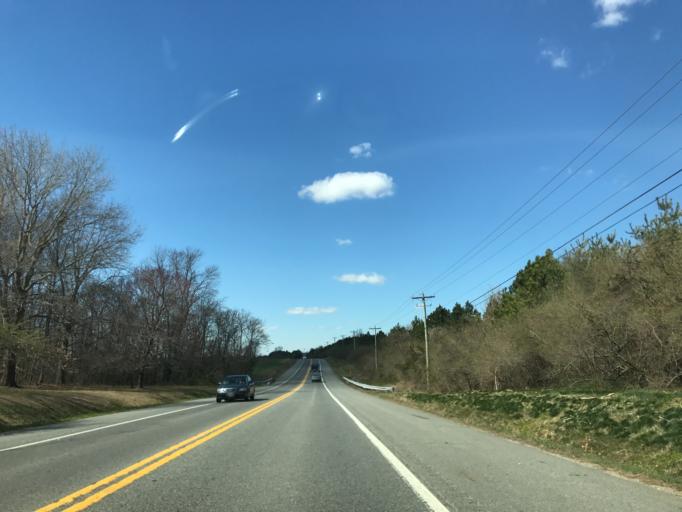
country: US
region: Maryland
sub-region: Queen Anne's County
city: Kingstown
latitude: 39.1814
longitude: -76.0052
